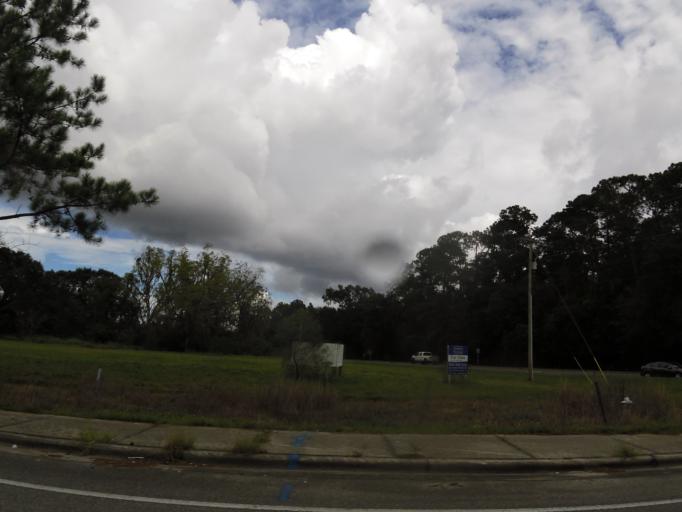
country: US
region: Florida
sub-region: Clay County
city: Lakeside
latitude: 30.1064
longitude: -81.7975
